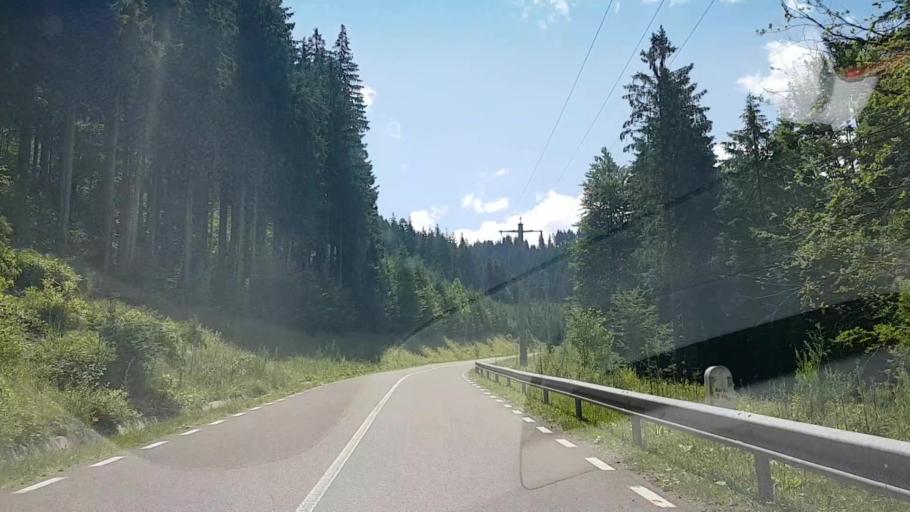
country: RO
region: Suceava
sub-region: Comuna Sadova
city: Sadova
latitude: 47.4690
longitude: 25.5135
